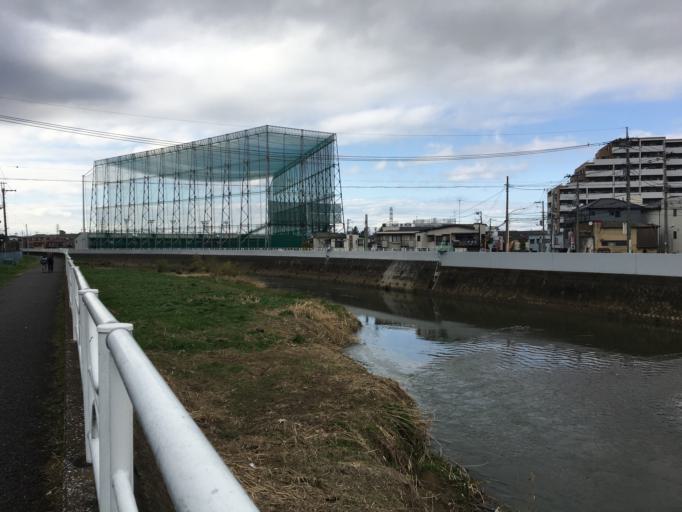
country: JP
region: Saitama
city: Shiki
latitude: 35.8359
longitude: 139.5794
